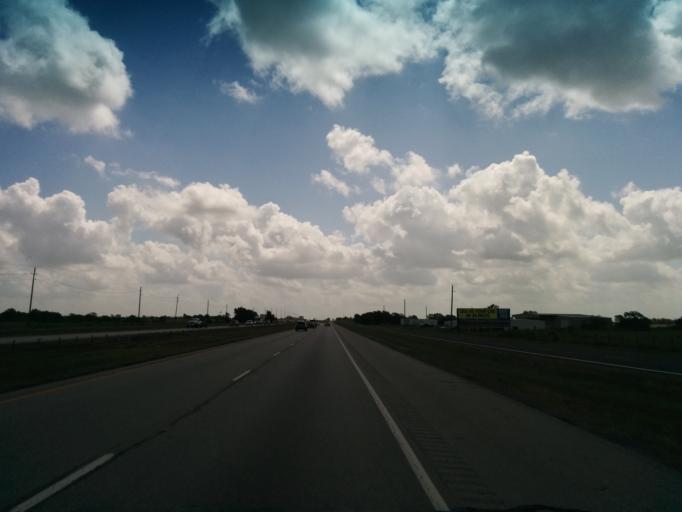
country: US
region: Texas
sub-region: Austin County
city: Sealy
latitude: 29.7554
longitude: -96.2443
